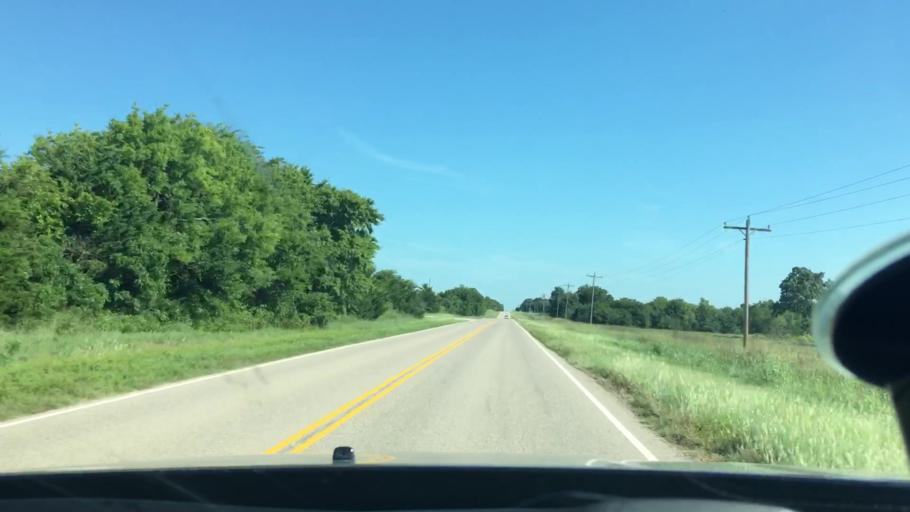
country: US
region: Oklahoma
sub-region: Johnston County
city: Tishomingo
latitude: 34.3764
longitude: -96.6361
